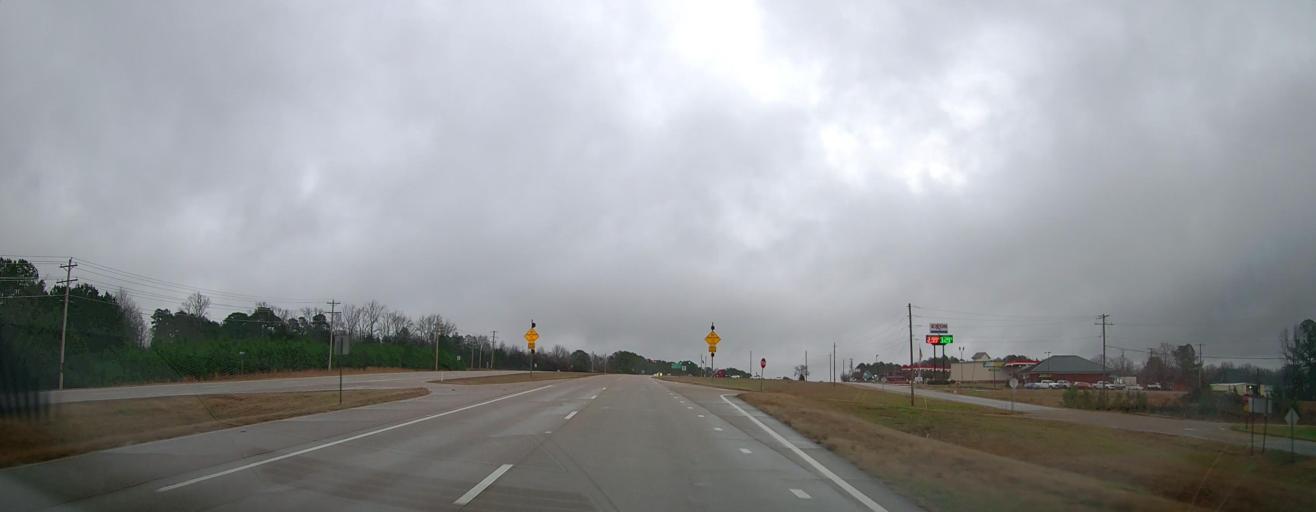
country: US
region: Mississippi
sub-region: Tippah County
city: Ripley
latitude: 34.9514
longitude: -88.9060
